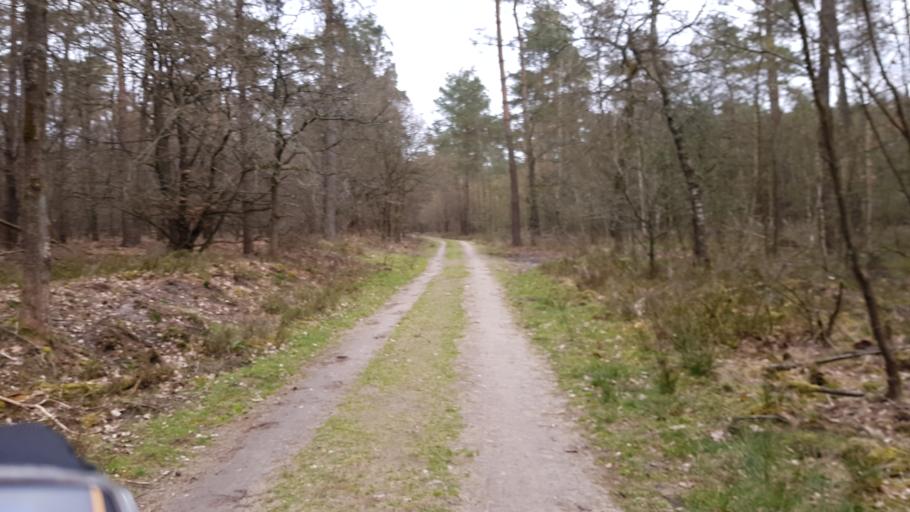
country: NL
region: Gelderland
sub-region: Gemeente Epe
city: Vaassen
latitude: 52.2978
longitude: 5.9137
